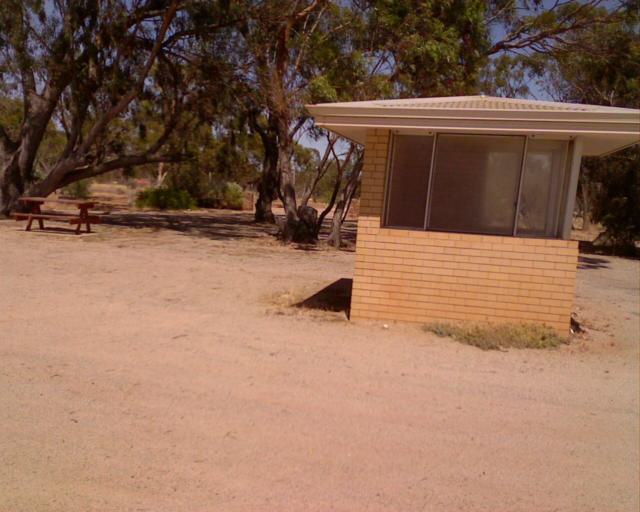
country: AU
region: Western Australia
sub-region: Moora
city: Moora
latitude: -30.2952
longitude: 116.0625
